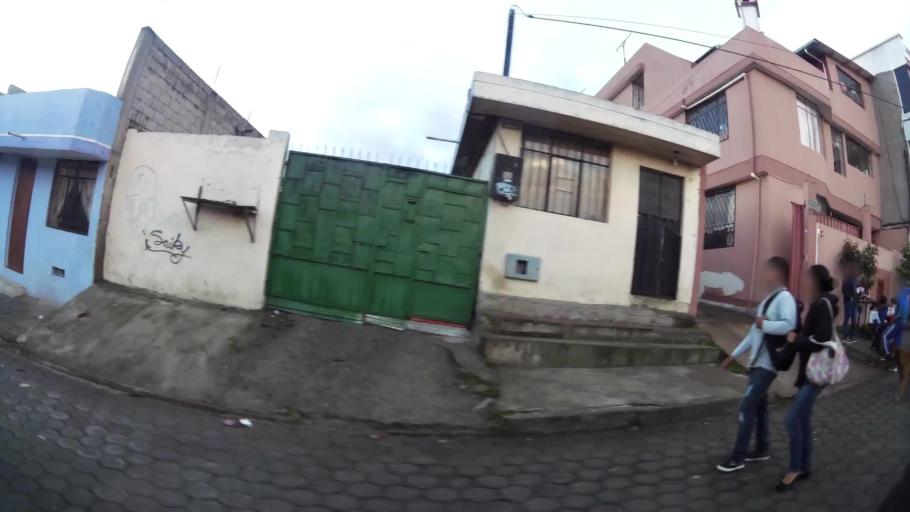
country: EC
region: Pichincha
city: Quito
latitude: -0.0977
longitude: -78.5185
